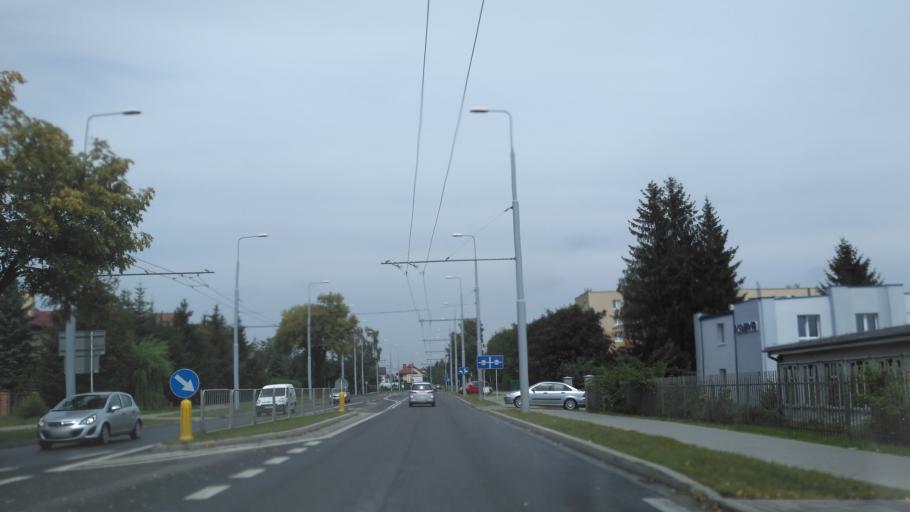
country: PL
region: Lublin Voivodeship
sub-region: Powiat lubelski
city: Lublin
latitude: 51.2012
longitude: 22.5860
